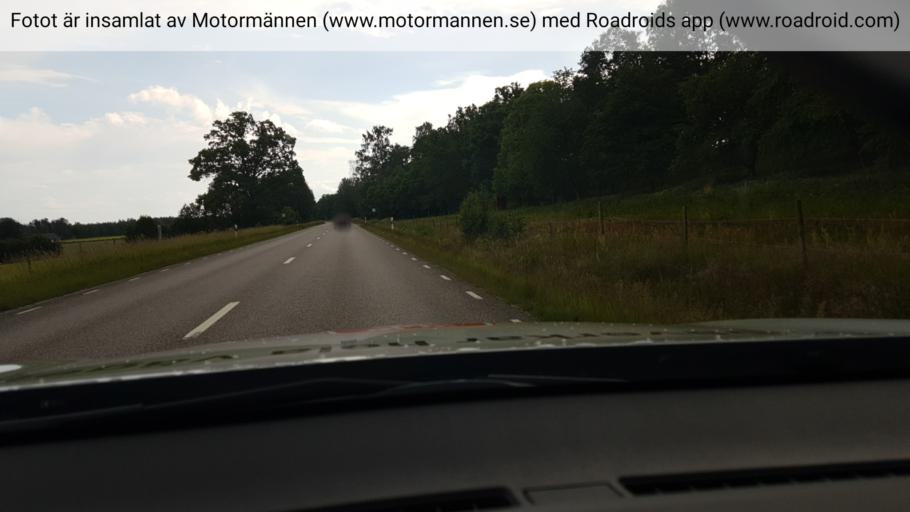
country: SE
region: Vaestra Goetaland
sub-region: Hjo Kommun
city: Hjo
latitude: 58.1476
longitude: 14.2152
